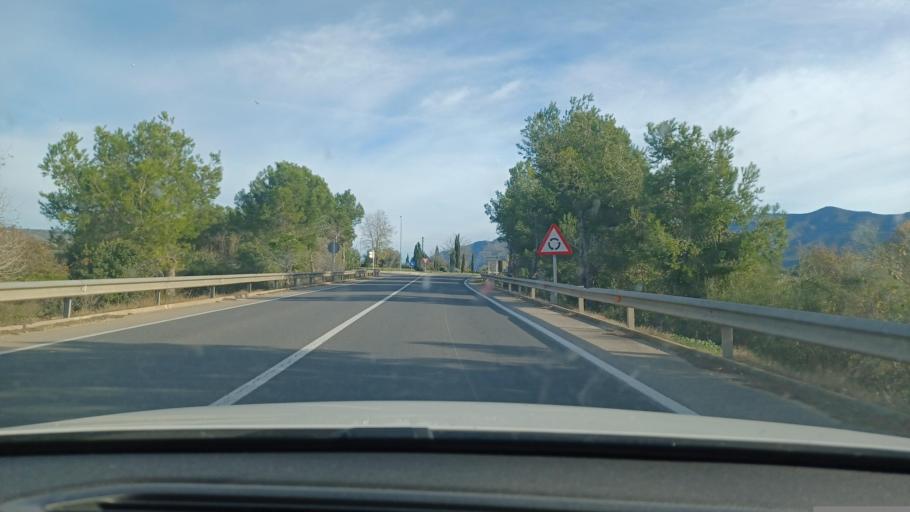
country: ES
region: Catalonia
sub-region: Provincia de Tarragona
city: Ulldecona
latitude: 40.5976
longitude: 0.4531
